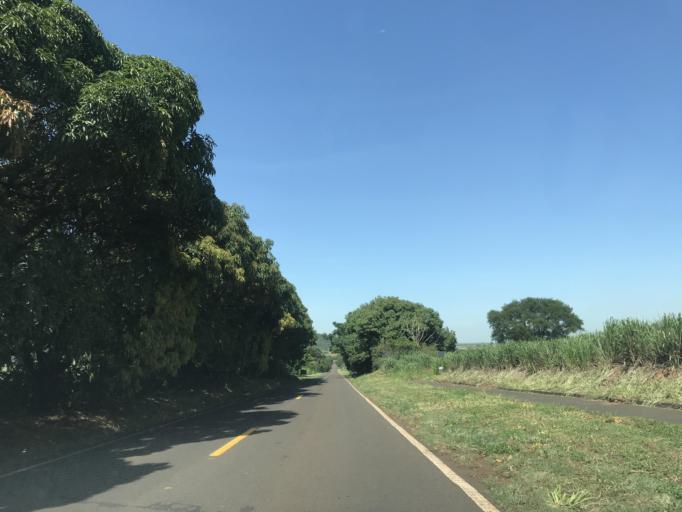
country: BR
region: Parana
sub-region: Terra Rica
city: Terra Rica
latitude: -22.7631
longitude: -52.6370
